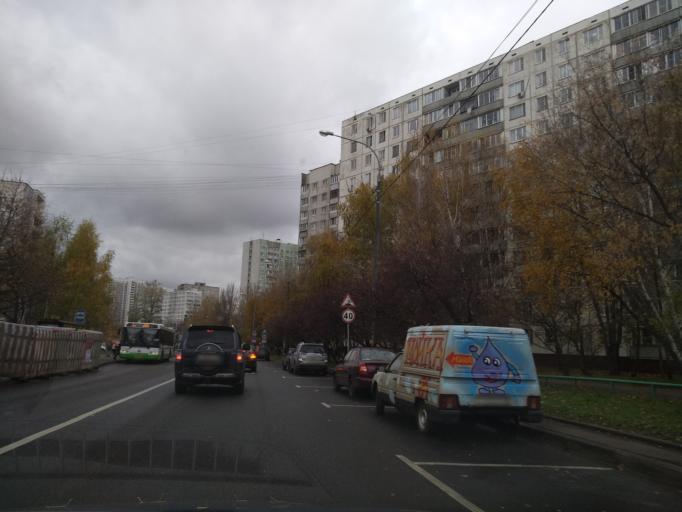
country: RU
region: Moscow
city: Bibirevo
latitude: 55.8885
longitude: 37.5989
